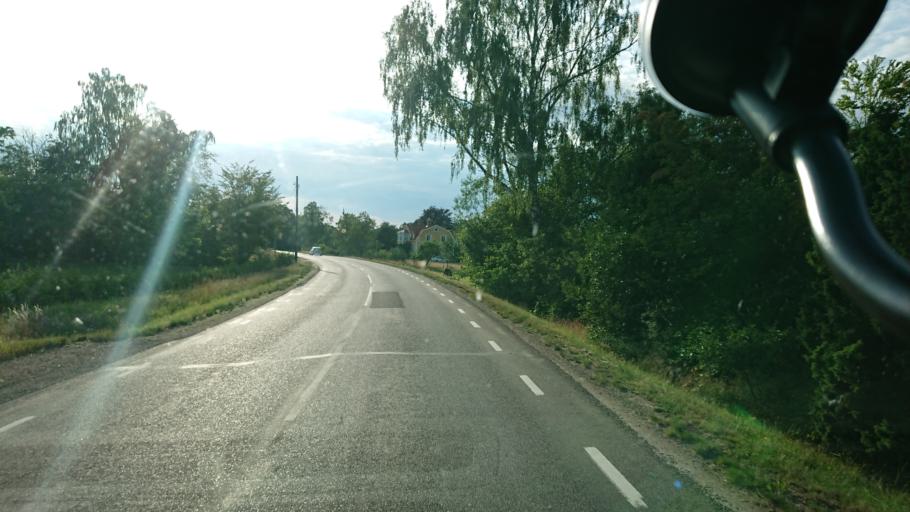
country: SE
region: Kronoberg
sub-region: Vaxjo Kommun
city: Braas
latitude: 57.0206
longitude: 15.0391
